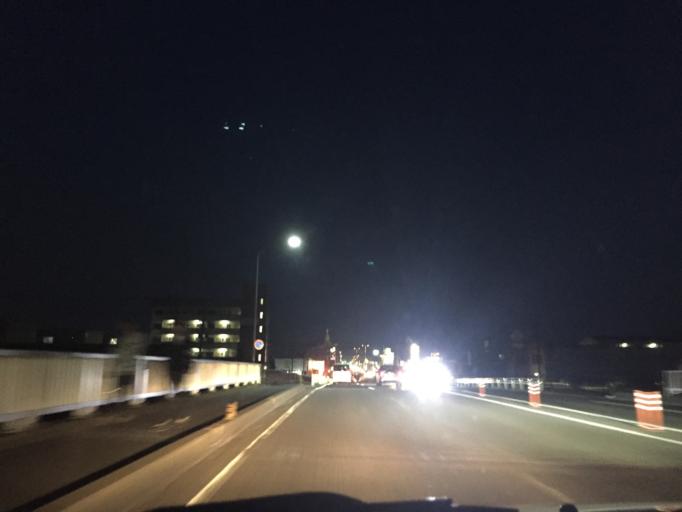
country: JP
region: Gifu
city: Ogaki
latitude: 35.3300
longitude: 136.6205
